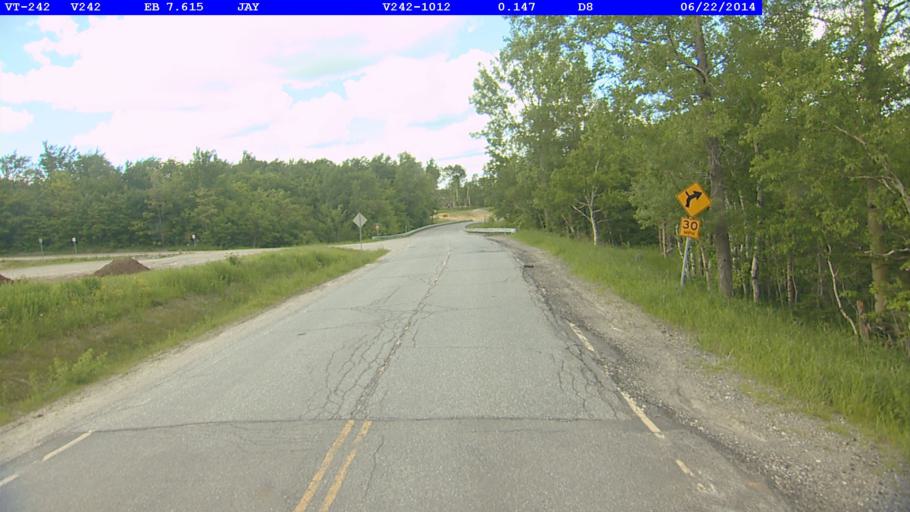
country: US
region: Vermont
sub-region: Franklin County
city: Richford
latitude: 44.9277
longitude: -72.5016
